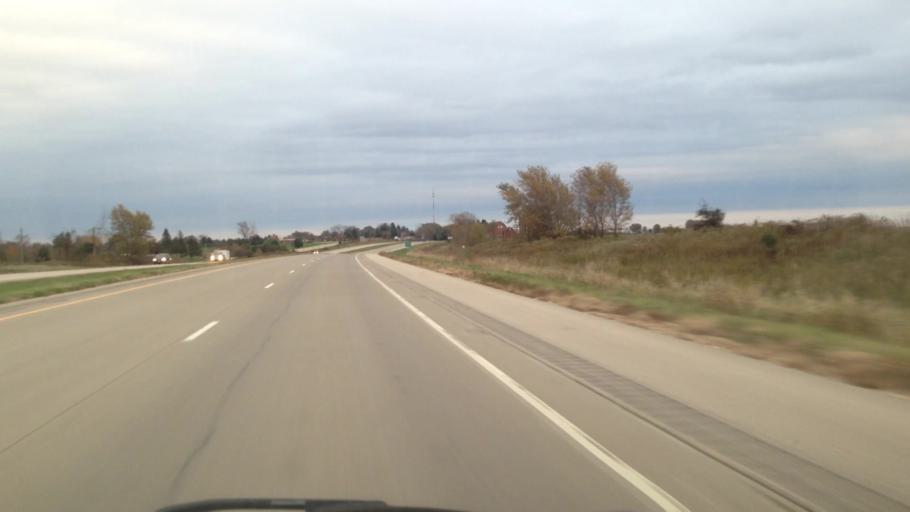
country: US
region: Minnesota
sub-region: Winona County
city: Winona
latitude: 43.9144
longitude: -91.5815
